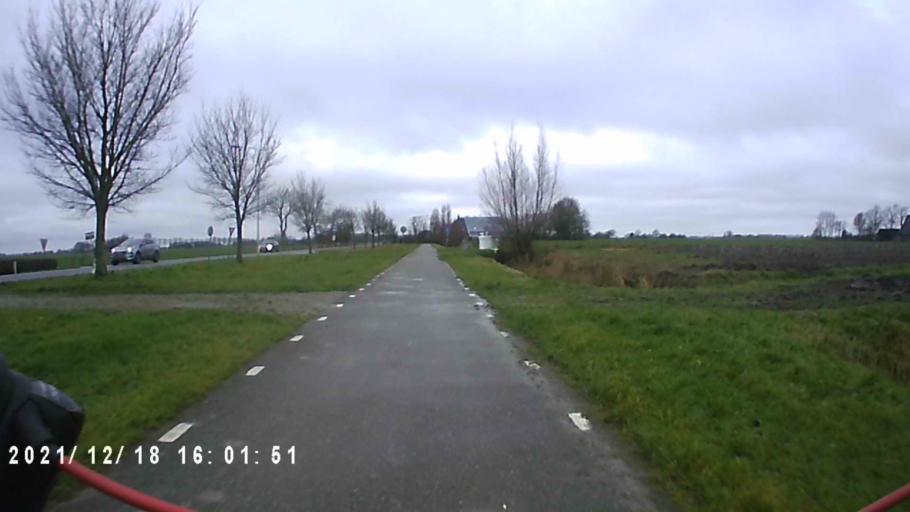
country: NL
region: Friesland
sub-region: Gemeente Dongeradeel
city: Anjum
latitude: 53.3459
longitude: 6.0850
